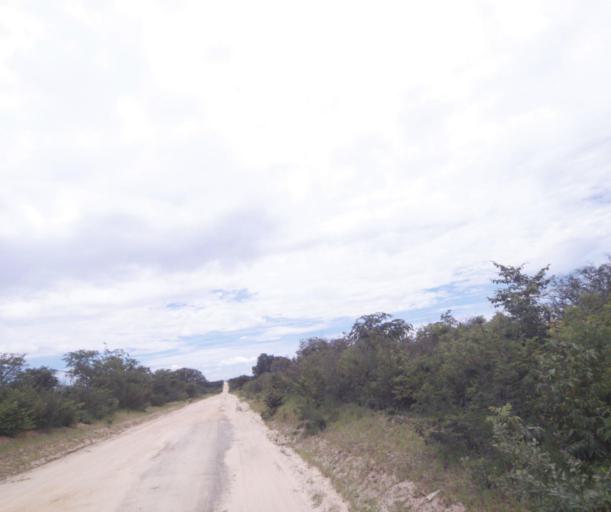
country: BR
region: Bahia
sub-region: Carinhanha
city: Carinhanha
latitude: -14.2335
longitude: -43.8608
